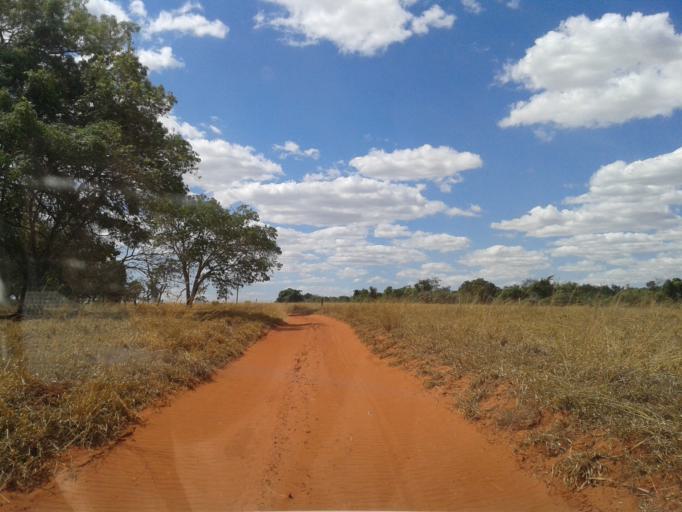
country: BR
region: Minas Gerais
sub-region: Centralina
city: Centralina
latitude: -18.7760
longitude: -49.0900
